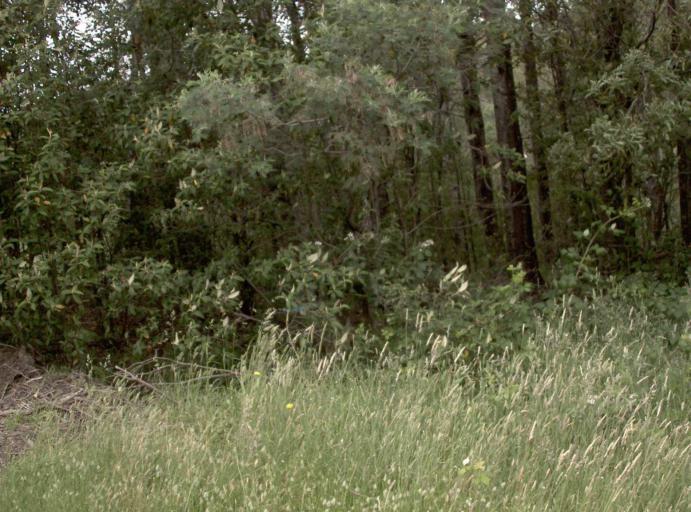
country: AU
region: Victoria
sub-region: Baw Baw
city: Warragul
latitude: -37.8865
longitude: 146.0910
